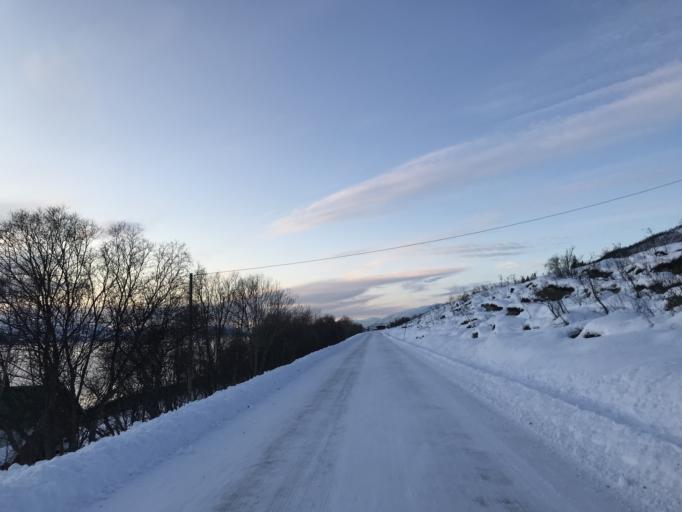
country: NO
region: Troms
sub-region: Karlsoy
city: Hansnes
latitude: 69.8464
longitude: 19.5354
